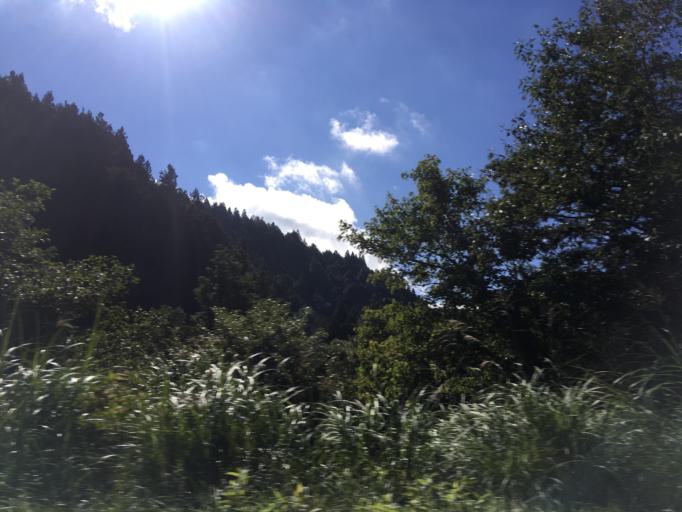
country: TW
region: Taiwan
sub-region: Yilan
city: Yilan
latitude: 24.5190
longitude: 121.5727
